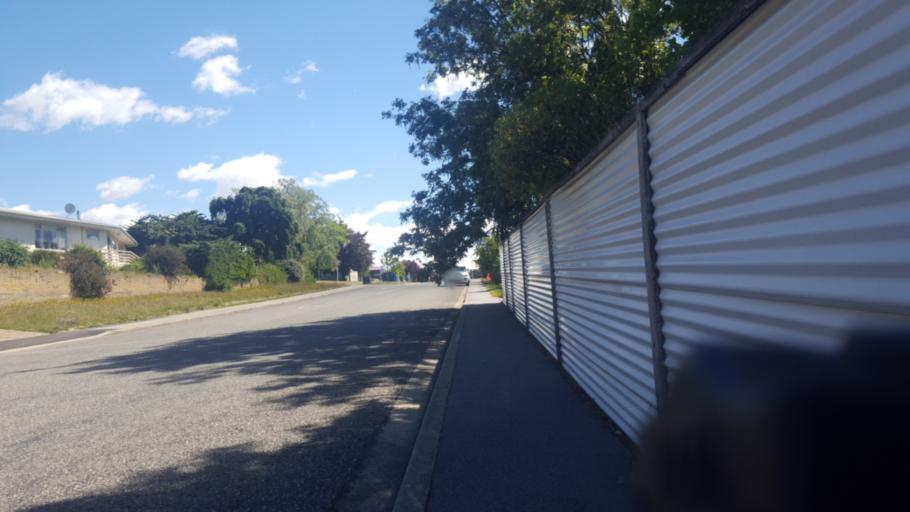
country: NZ
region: Otago
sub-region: Queenstown-Lakes District
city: Wanaka
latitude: -45.0462
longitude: 169.2043
